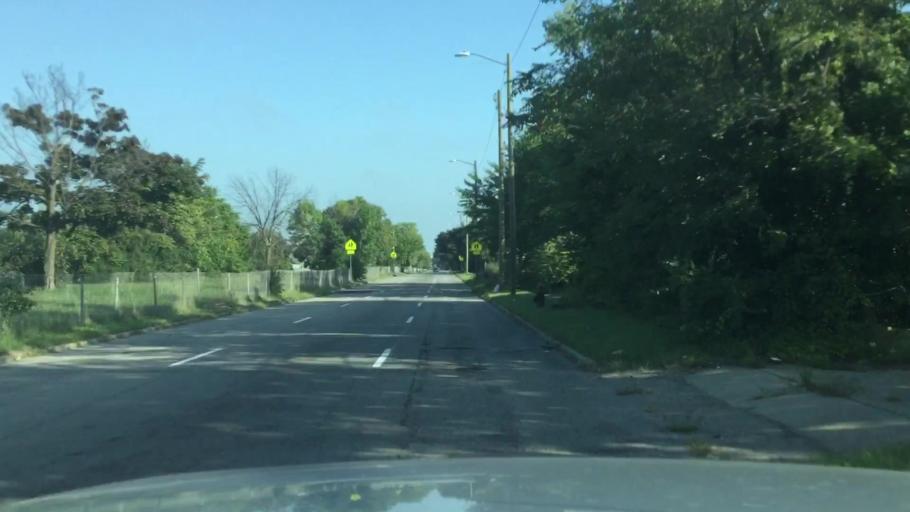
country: US
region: Michigan
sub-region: Oakland County
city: Hazel Park
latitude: 42.4360
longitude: -83.0943
